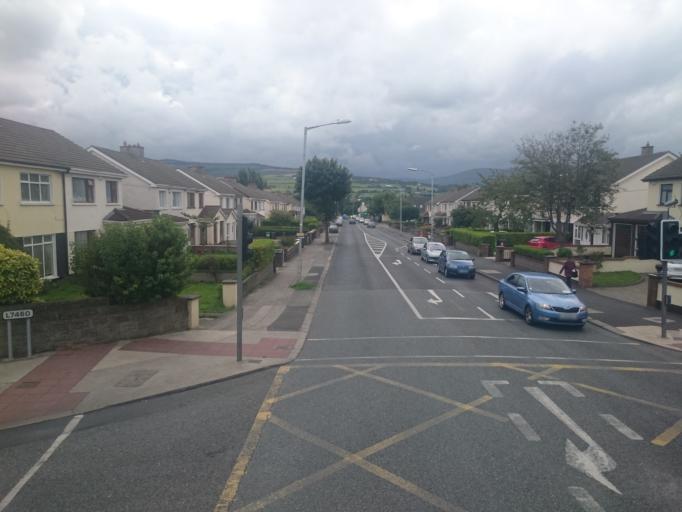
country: IE
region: Leinster
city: Oldbawn
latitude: 53.2803
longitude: -6.3586
